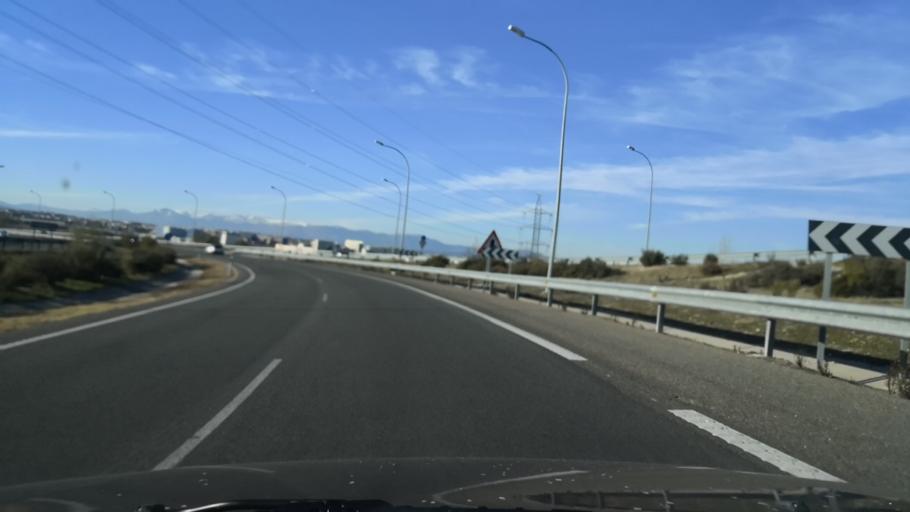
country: ES
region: Madrid
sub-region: Provincia de Madrid
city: San Sebastian de los Reyes
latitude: 40.5263
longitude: -3.5992
